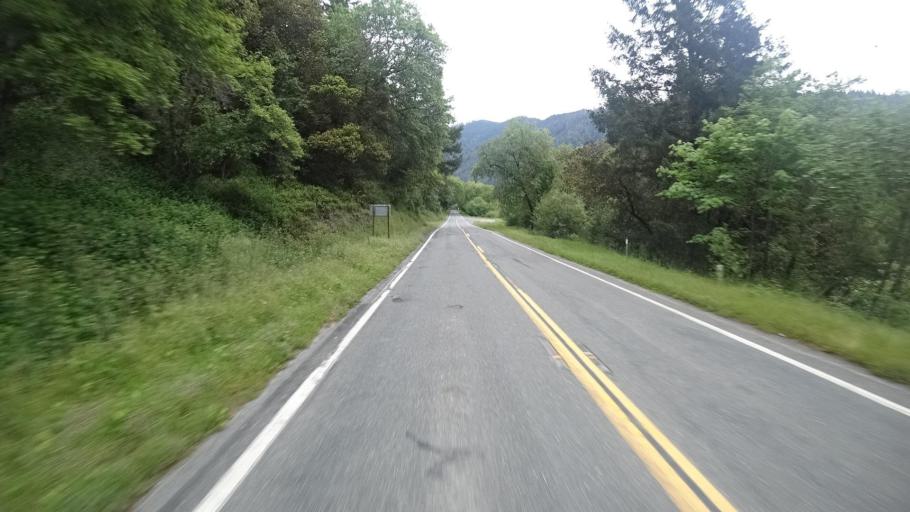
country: US
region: California
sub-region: Humboldt County
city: Willow Creek
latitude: 41.1881
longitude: -123.6967
